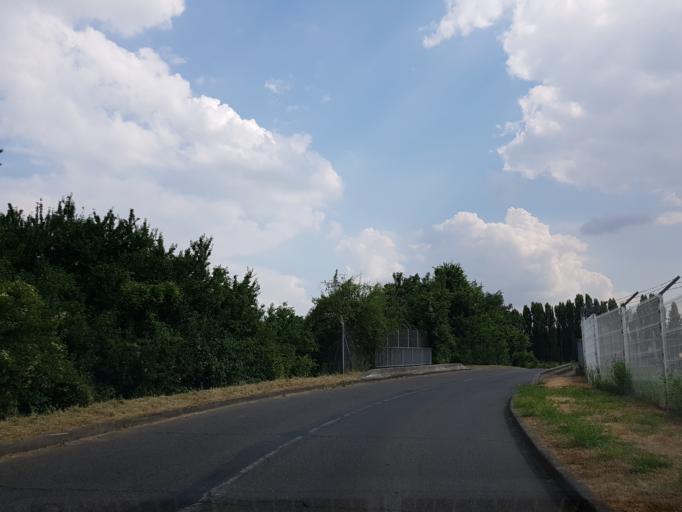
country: FR
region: Ile-de-France
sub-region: Departement de l'Essonne
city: Wissous
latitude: 48.7422
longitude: 2.3315
